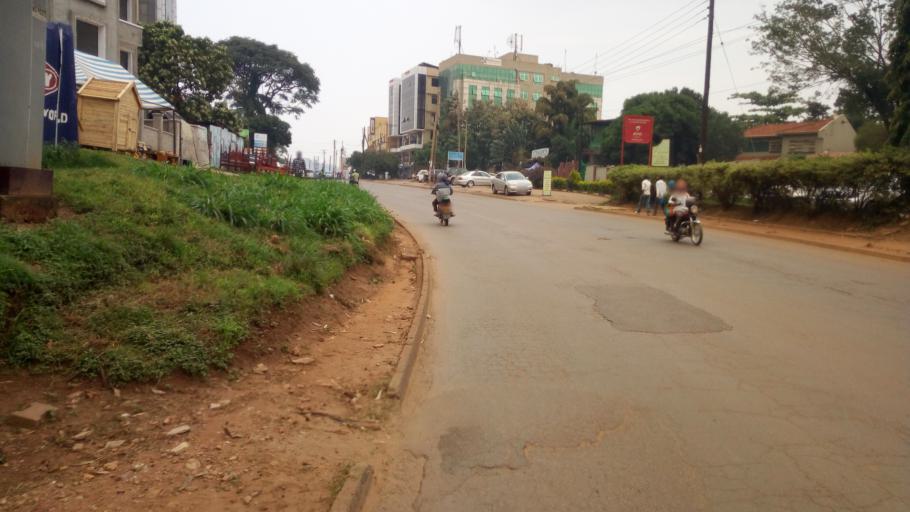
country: UG
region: Central Region
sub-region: Kampala District
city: Kampala
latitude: 0.3196
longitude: 32.6207
